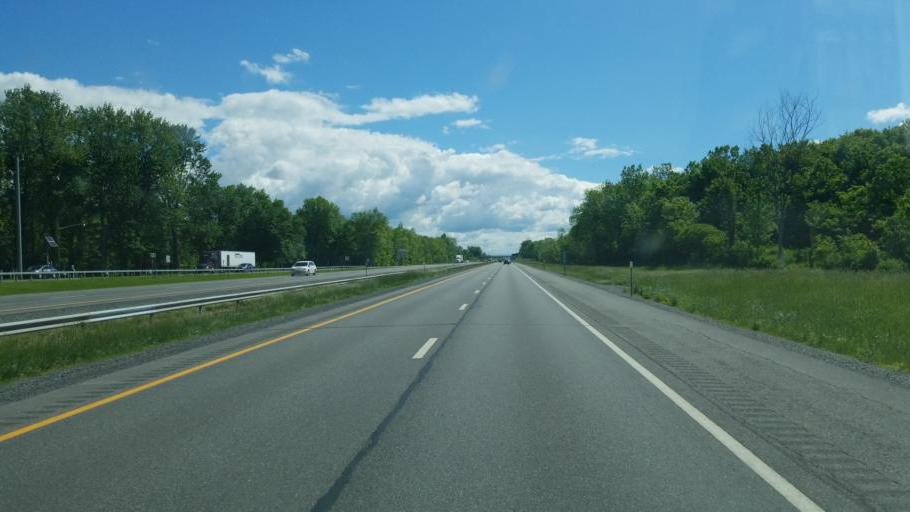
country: US
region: New York
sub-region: Madison County
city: Oneida
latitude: 43.1158
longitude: -75.6459
